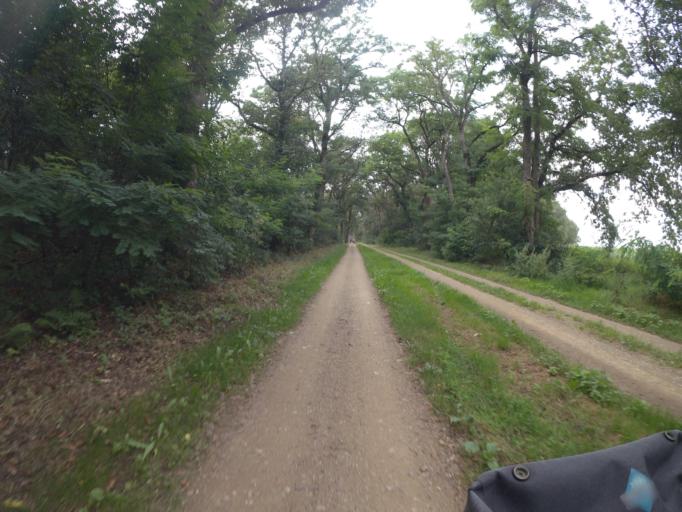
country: DE
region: North Rhine-Westphalia
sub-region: Regierungsbezirk Dusseldorf
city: Goch
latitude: 51.6279
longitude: 6.0647
